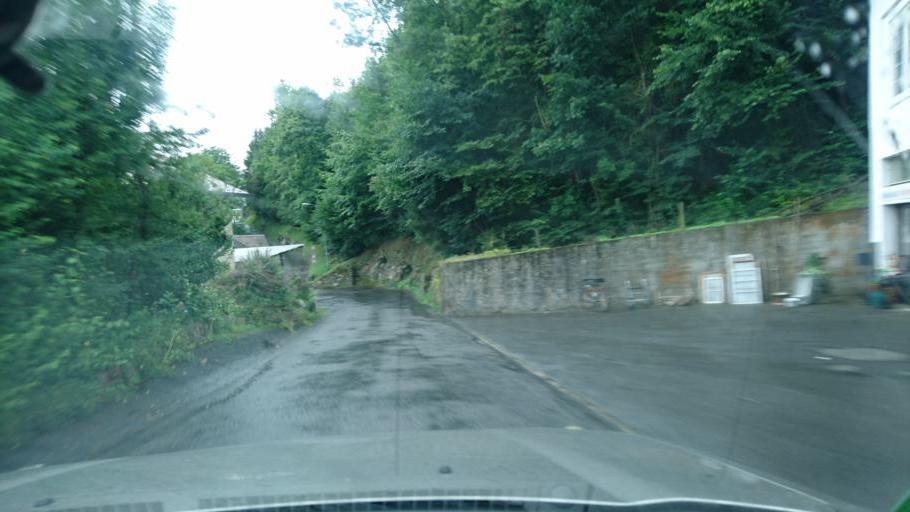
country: CH
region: Saint Gallen
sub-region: Wahlkreis See-Gaster
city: Amden
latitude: 47.1156
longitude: 9.1728
